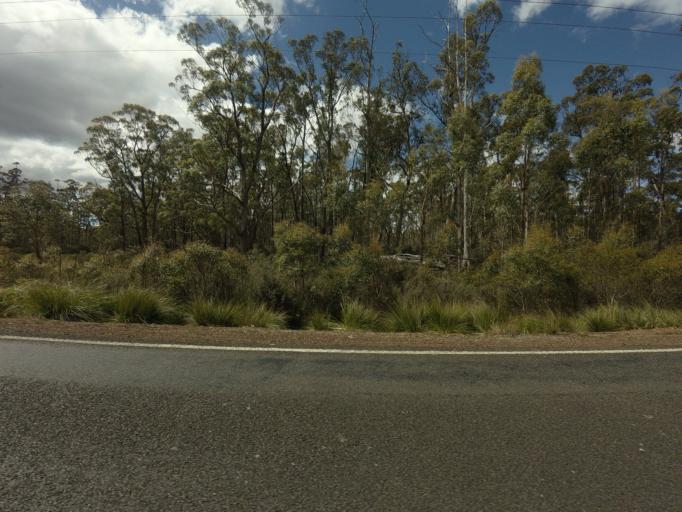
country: AU
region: Tasmania
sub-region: Northern Midlands
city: Evandale
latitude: -42.0213
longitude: 147.7453
